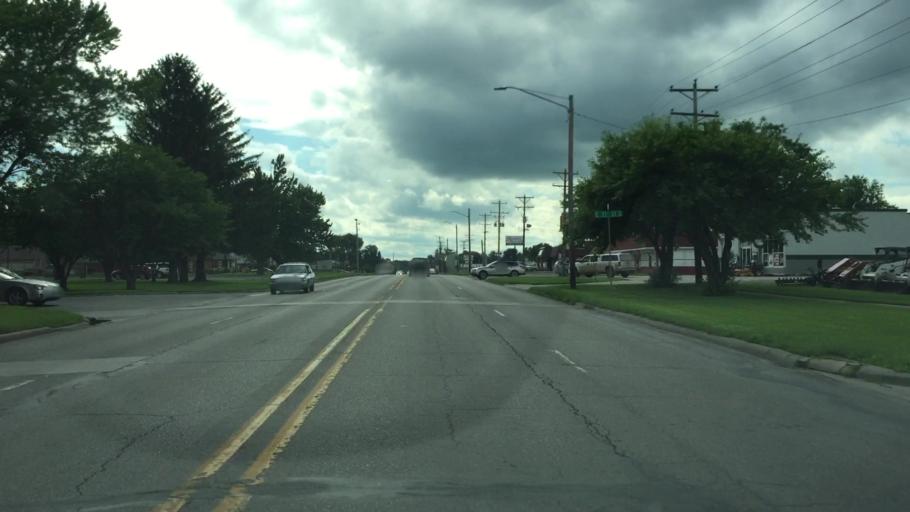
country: US
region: Iowa
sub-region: Jasper County
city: Newton
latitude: 41.6992
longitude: -93.0251
